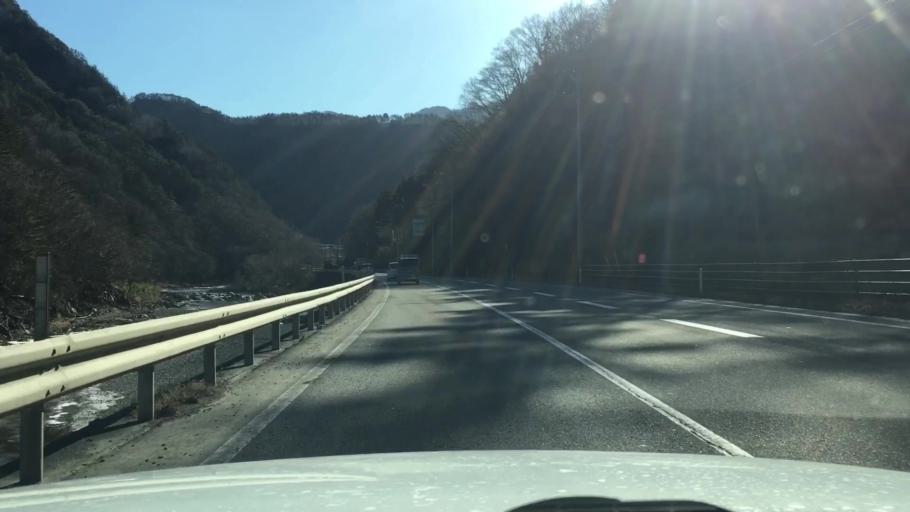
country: JP
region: Iwate
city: Miyako
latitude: 39.6140
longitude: 141.7885
